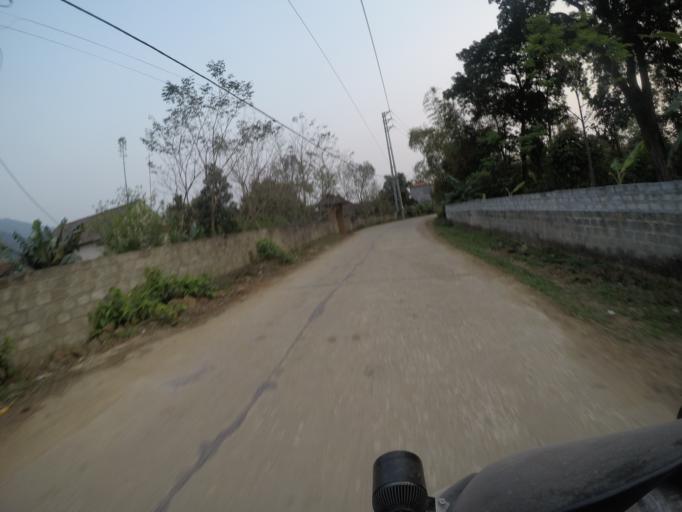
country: VN
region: Vinh Phuc
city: Trai Ngau
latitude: 21.4666
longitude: 105.5710
